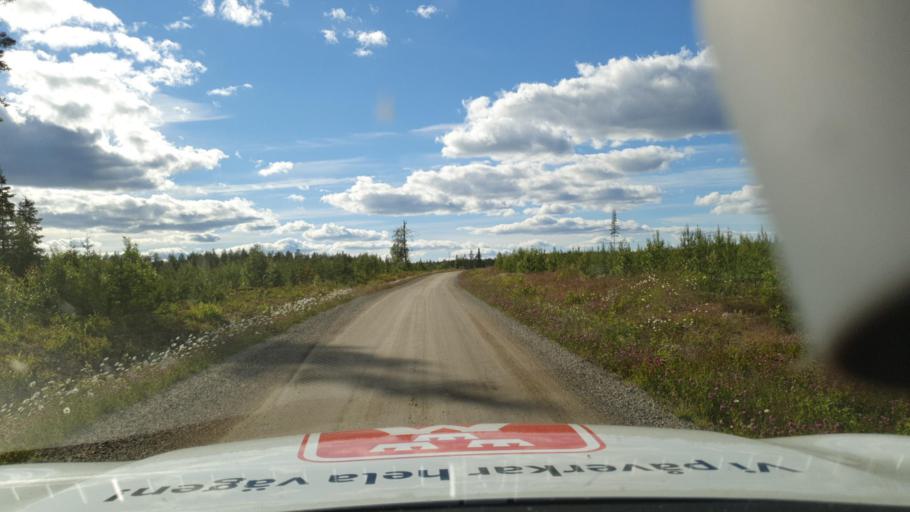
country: SE
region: Vaesterbotten
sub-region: Lycksele Kommun
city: Lycksele
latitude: 64.4016
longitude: 18.5649
